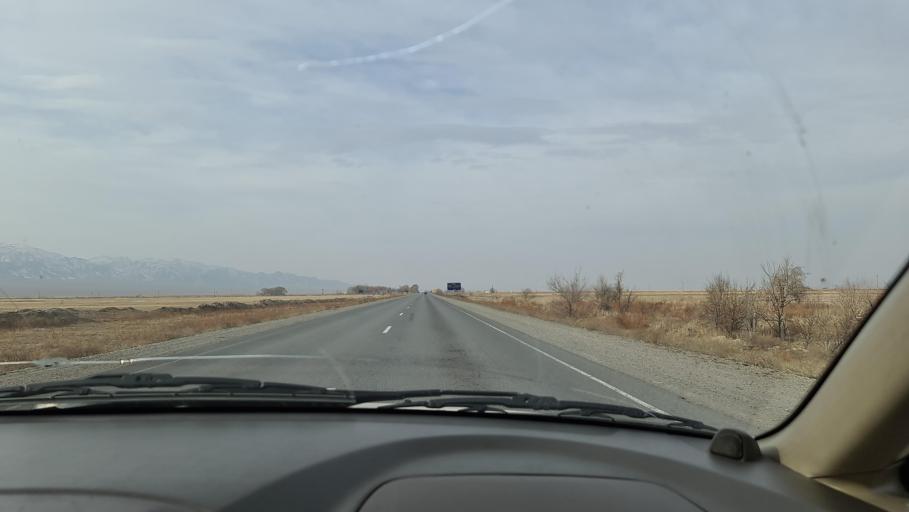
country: KG
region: Chuy
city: Tokmok
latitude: 43.3485
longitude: 75.4909
